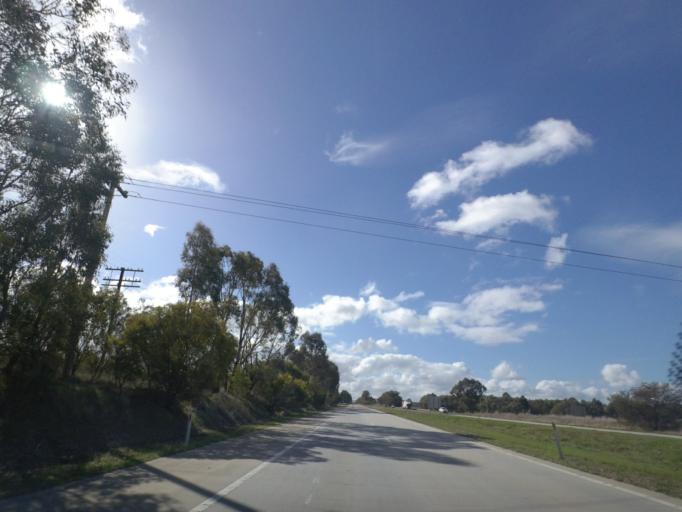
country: AU
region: New South Wales
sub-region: Albury Municipality
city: Lavington
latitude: -35.9920
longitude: 146.9946
